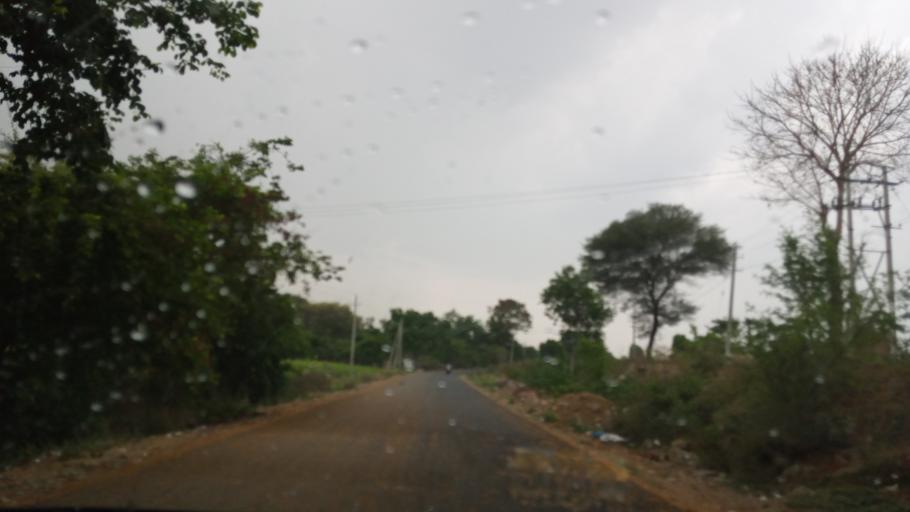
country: IN
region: Karnataka
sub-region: Kolar
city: Mulbagal
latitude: 13.1054
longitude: 78.3271
